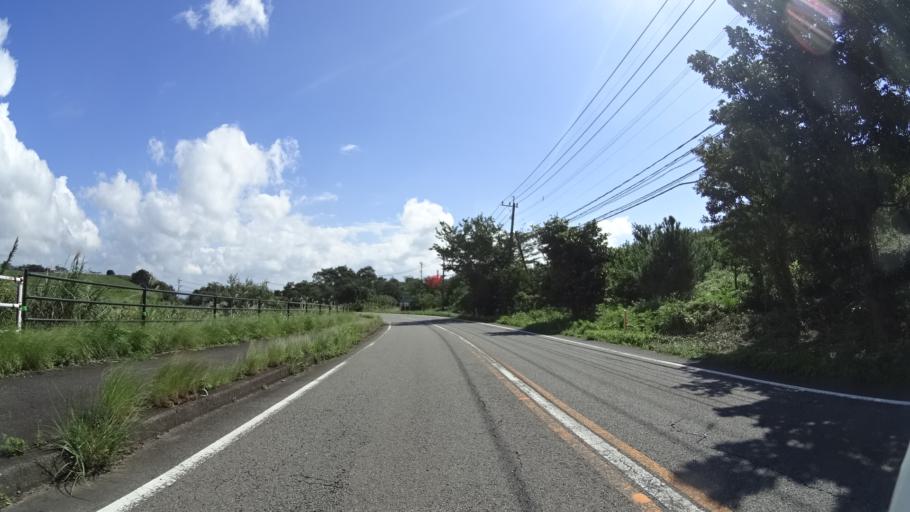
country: JP
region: Oita
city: Beppu
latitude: 33.3304
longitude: 131.4568
